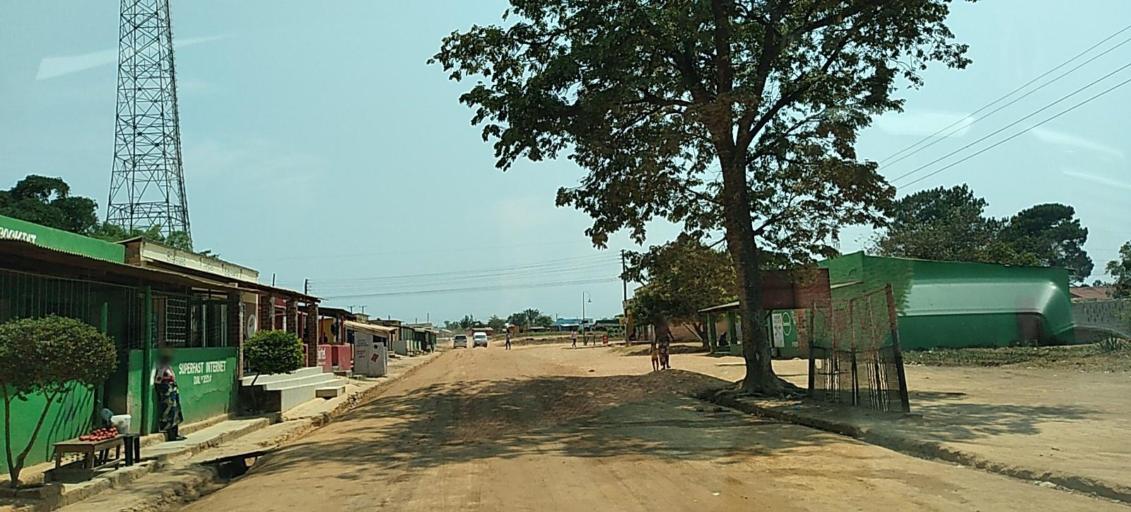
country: ZM
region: Copperbelt
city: Chingola
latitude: -12.5978
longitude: 27.9567
